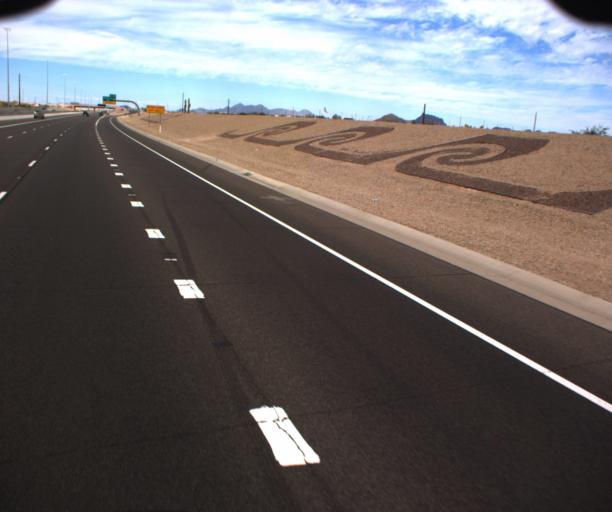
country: US
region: Arizona
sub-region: Pinal County
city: Apache Junction
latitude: 33.4450
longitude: -111.6620
